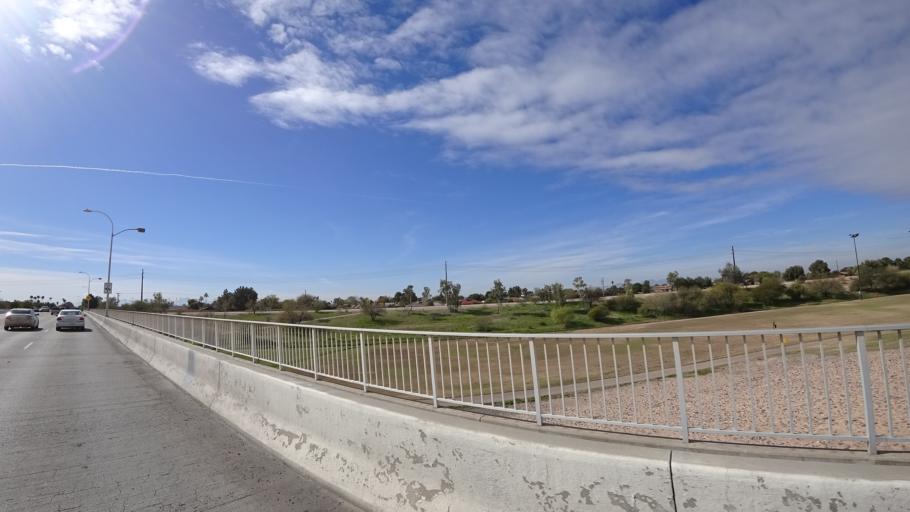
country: US
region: Arizona
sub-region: Maricopa County
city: Peoria
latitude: 33.6078
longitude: -112.1860
